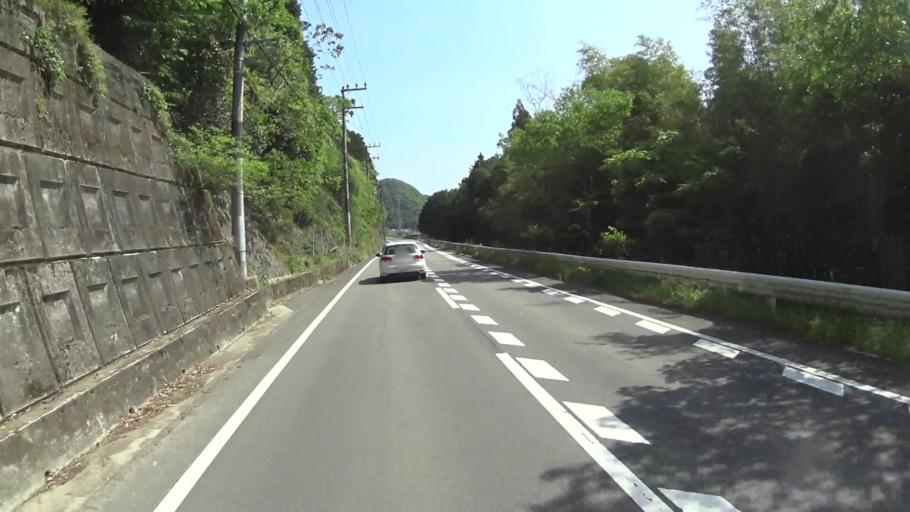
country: JP
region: Kyoto
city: Kameoka
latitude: 35.1151
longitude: 135.5182
